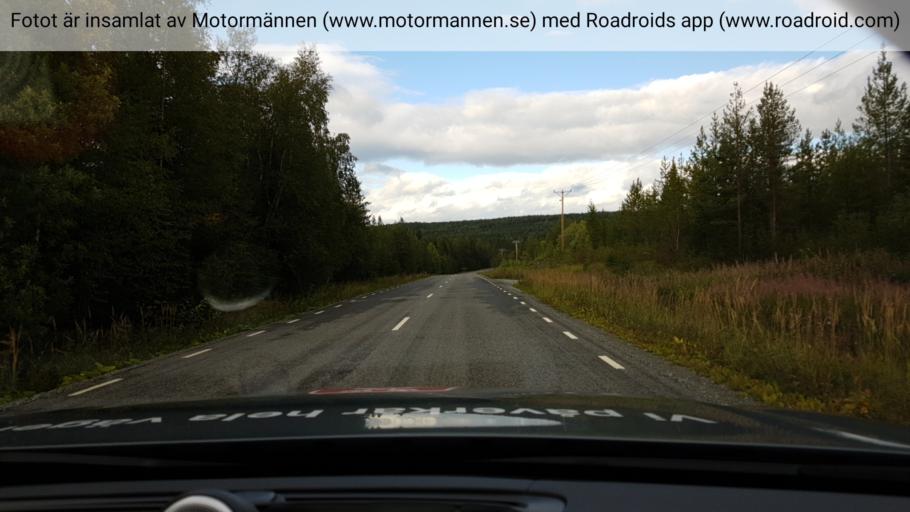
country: SE
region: Jaemtland
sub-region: Krokoms Kommun
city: Krokom
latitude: 63.6715
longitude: 14.5586
